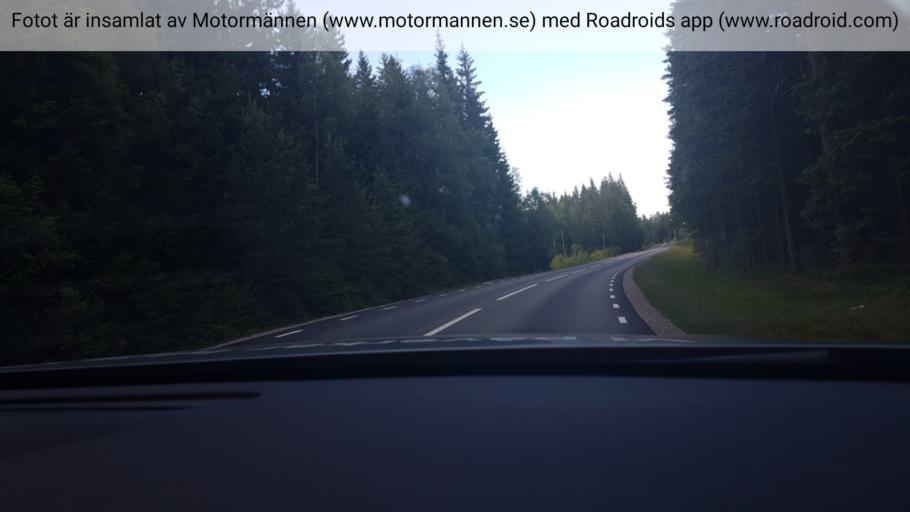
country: SE
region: Joenkoeping
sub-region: Gnosjo Kommun
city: Gnosjoe
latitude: 57.5664
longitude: 13.6202
